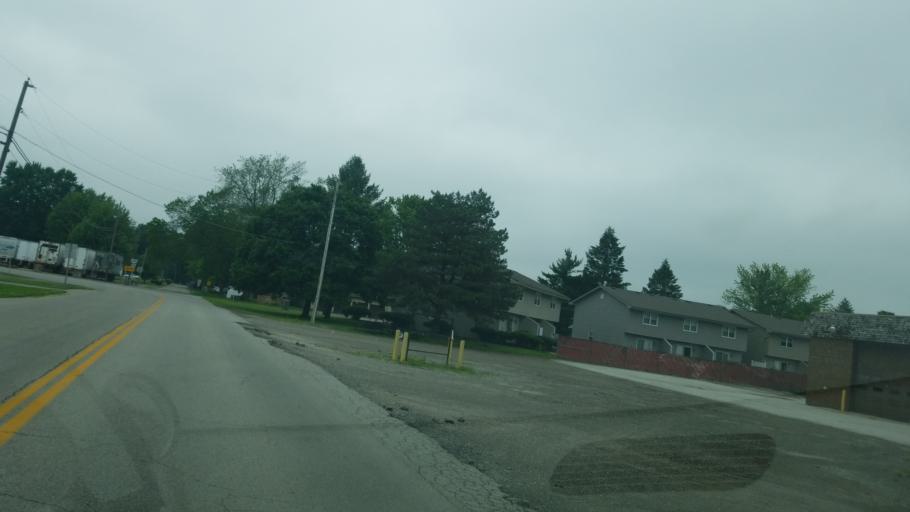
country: US
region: Ohio
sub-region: Wyandot County
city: Upper Sandusky
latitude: 40.8160
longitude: -83.2794
